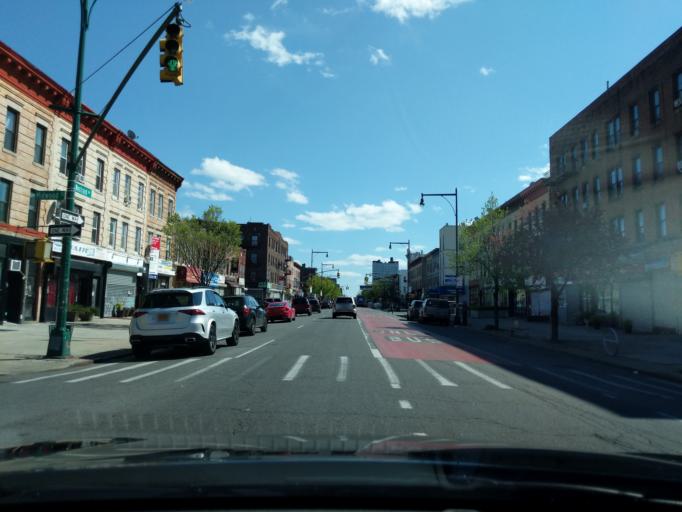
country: US
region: New York
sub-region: Kings County
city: Brooklyn
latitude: 40.6602
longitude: -73.9505
